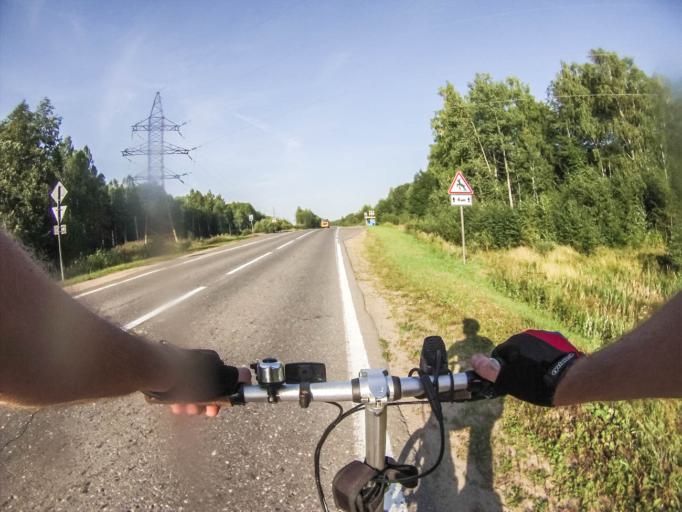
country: RU
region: Jaroslavl
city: Uglich
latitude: 57.6800
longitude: 38.3177
